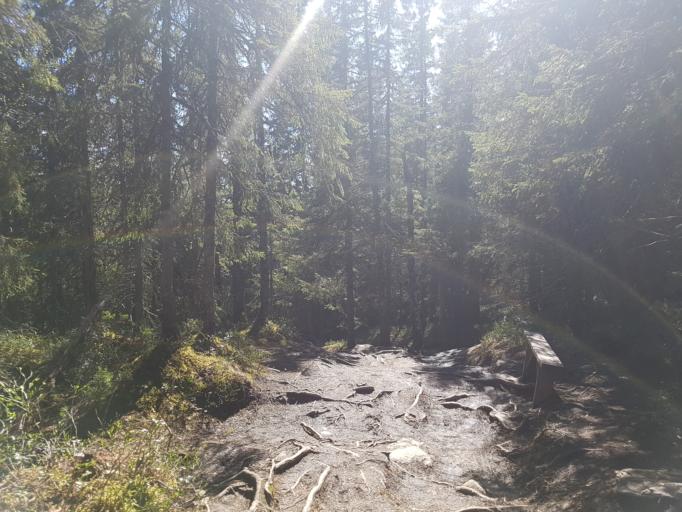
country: NO
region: Sor-Trondelag
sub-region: Trondheim
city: Trondheim
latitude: 63.4294
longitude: 10.3120
